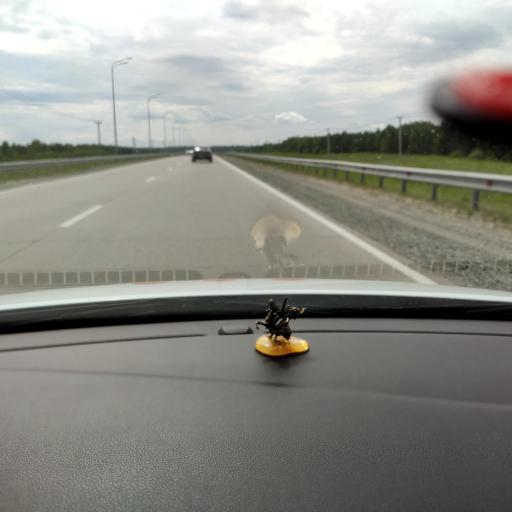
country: RU
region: Tatarstan
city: Stolbishchi
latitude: 55.6758
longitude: 49.1851
